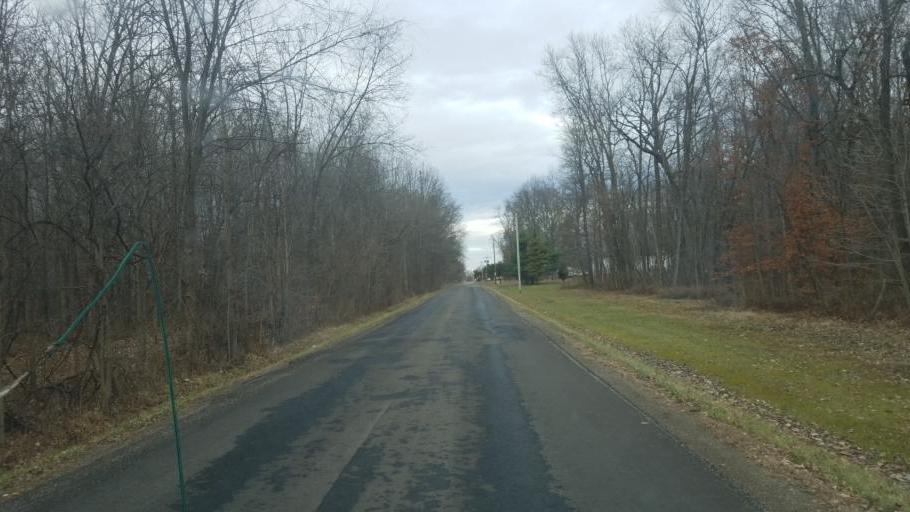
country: US
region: Ohio
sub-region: Morrow County
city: Cardington
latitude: 40.4859
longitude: -82.8686
